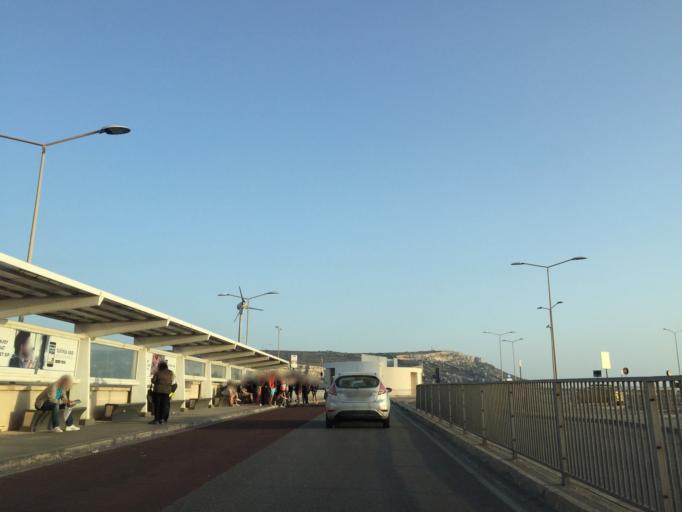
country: MT
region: Il-Mellieha
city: Mellieha
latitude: 35.9881
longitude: 14.3288
